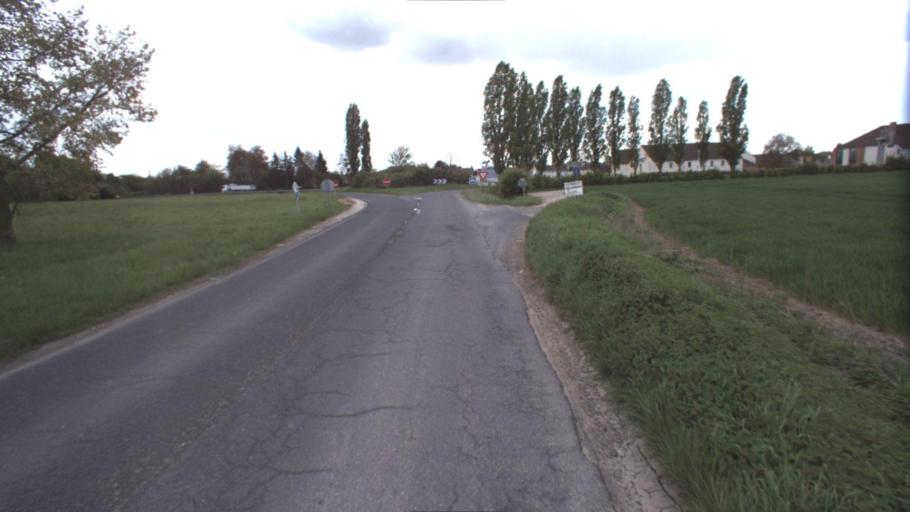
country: FR
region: Ile-de-France
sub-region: Departement de Seine-et-Marne
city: Rozay-en-Brie
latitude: 48.6887
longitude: 2.9655
